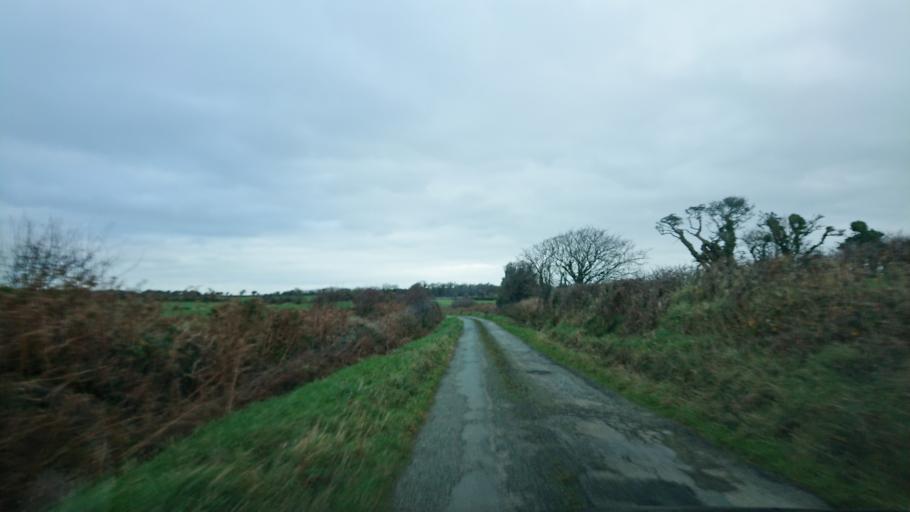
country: IE
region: Munster
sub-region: Waterford
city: Dunmore East
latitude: 52.1849
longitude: -7.0429
